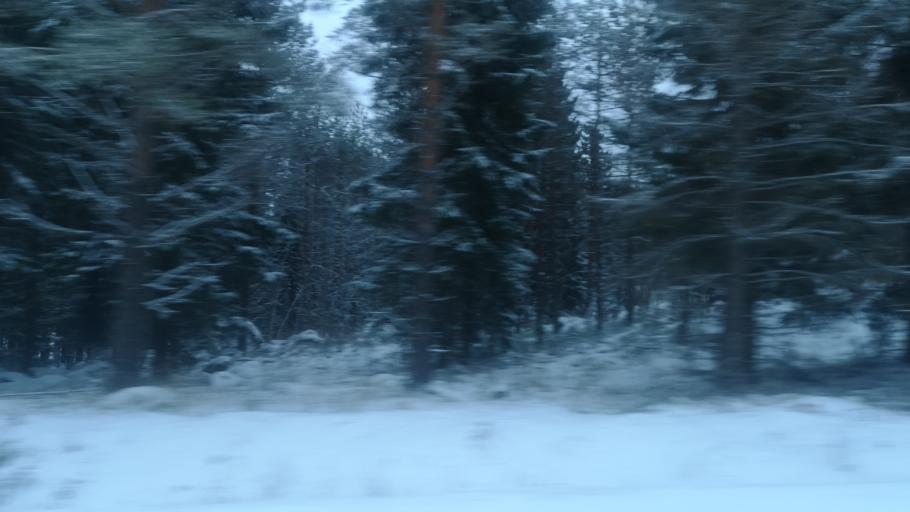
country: FI
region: Southern Savonia
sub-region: Savonlinna
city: Enonkoski
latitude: 62.0461
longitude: 28.7047
